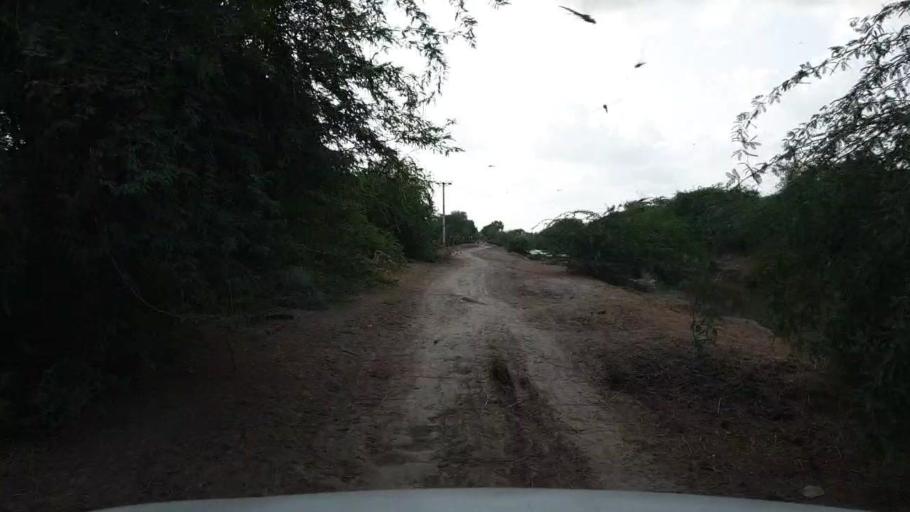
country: PK
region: Sindh
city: Kario
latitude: 24.7570
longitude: 68.6085
